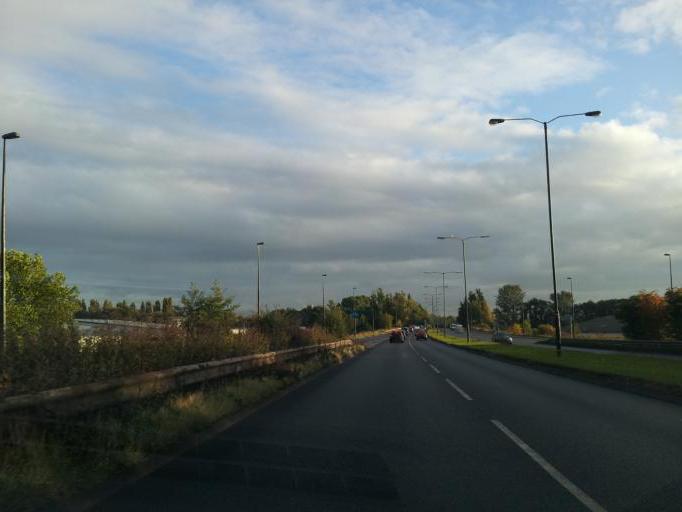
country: GB
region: England
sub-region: City and Borough of Salford
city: Eccles
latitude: 53.4634
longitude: -2.3335
